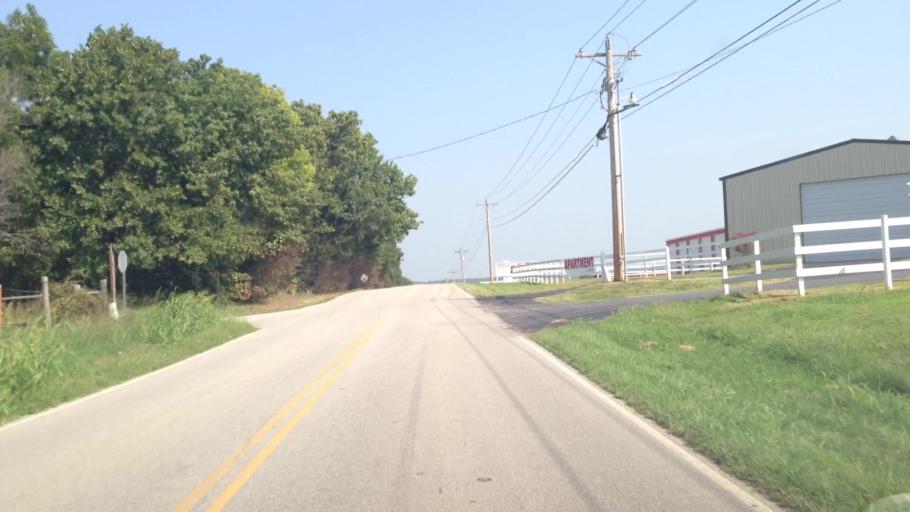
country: US
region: Oklahoma
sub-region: Delaware County
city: Cleora
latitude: 36.5570
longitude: -94.9708
